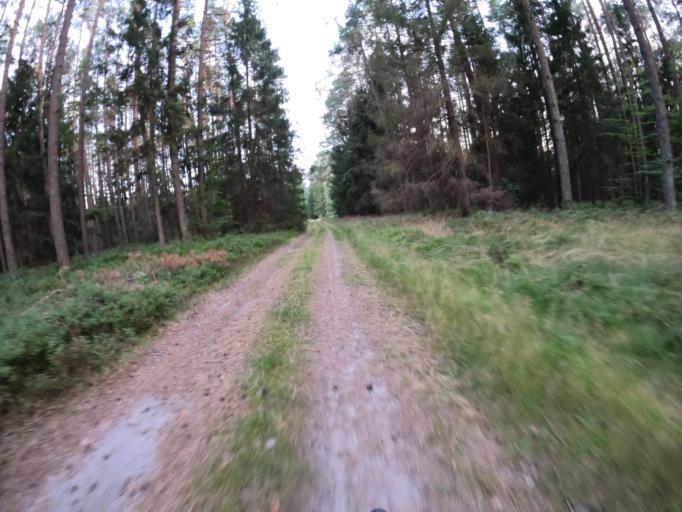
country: PL
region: West Pomeranian Voivodeship
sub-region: Powiat koszalinski
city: Sianow
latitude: 54.0904
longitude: 16.4084
